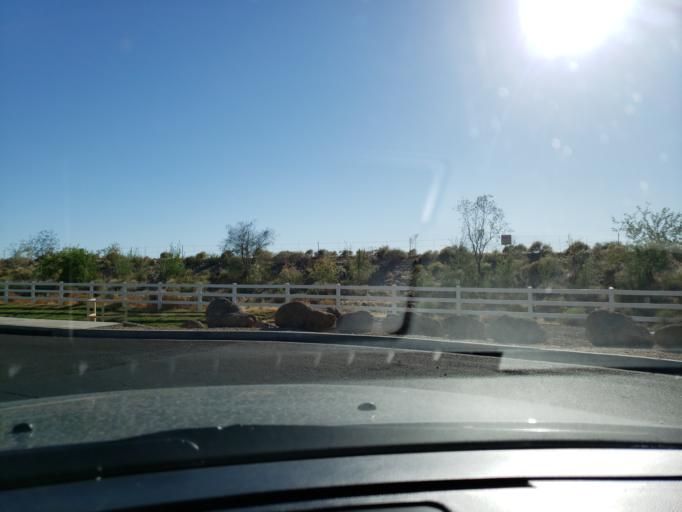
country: US
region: Arizona
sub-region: Maricopa County
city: Youngtown
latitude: 33.5780
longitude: -112.3114
